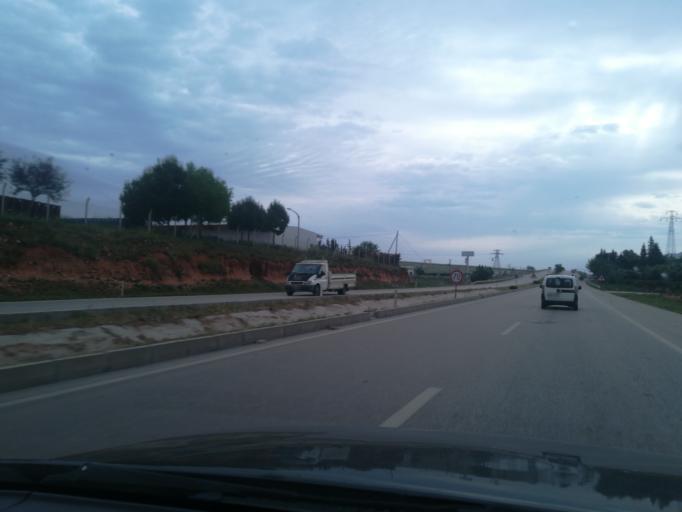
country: TR
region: Adana
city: Yakapinar
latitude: 36.9655
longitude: 35.6233
